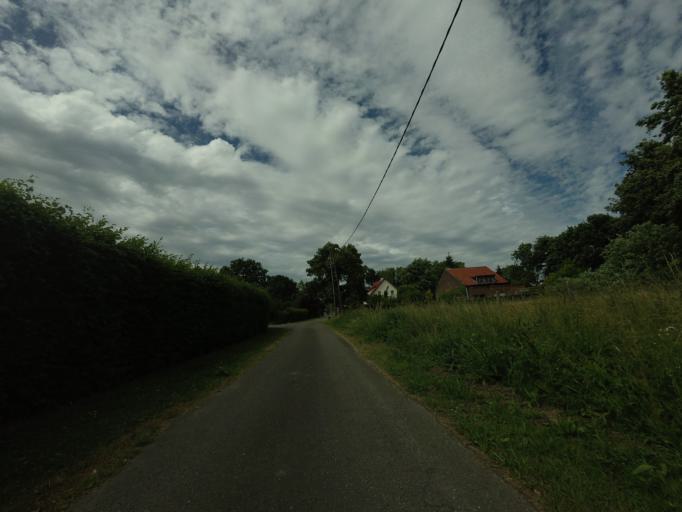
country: BE
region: Flanders
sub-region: Provincie Antwerpen
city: Rumst
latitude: 51.0840
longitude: 4.4609
